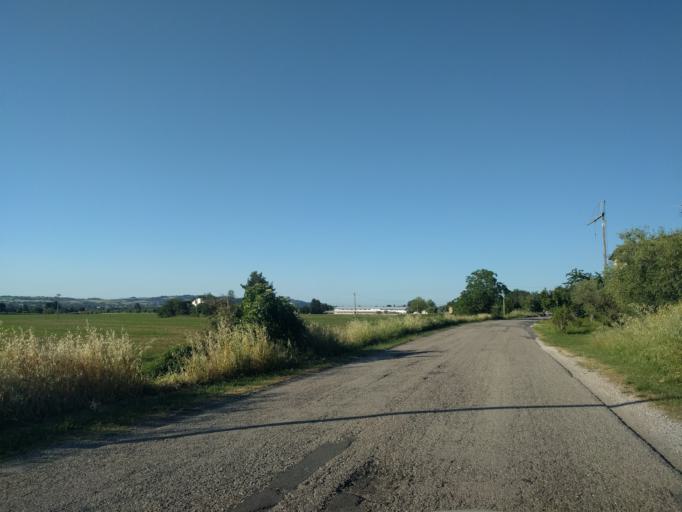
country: IT
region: The Marches
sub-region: Provincia di Pesaro e Urbino
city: Montemaggiore al Metauro
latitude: 43.7411
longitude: 12.9442
